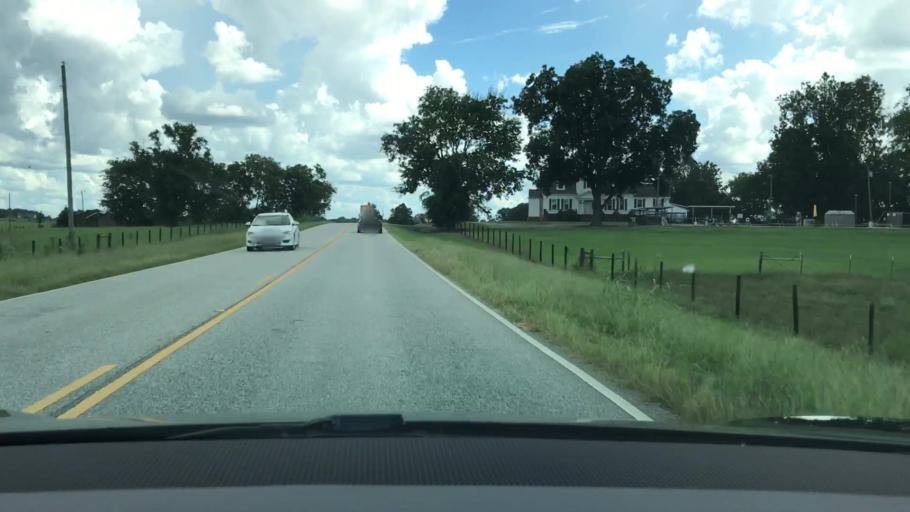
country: US
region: Alabama
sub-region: Montgomery County
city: Pike Road
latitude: 32.2611
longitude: -86.0989
